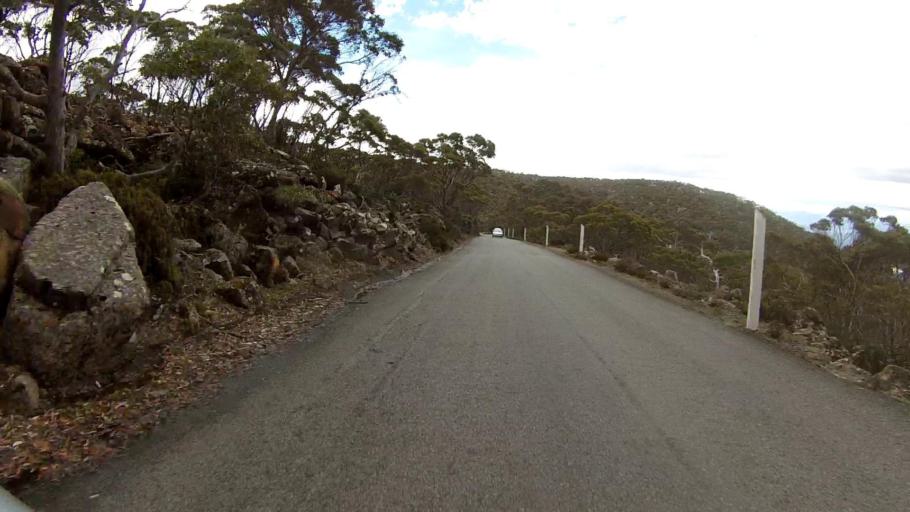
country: AU
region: Tasmania
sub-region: Glenorchy
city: West Moonah
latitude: -42.8876
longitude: 147.2208
